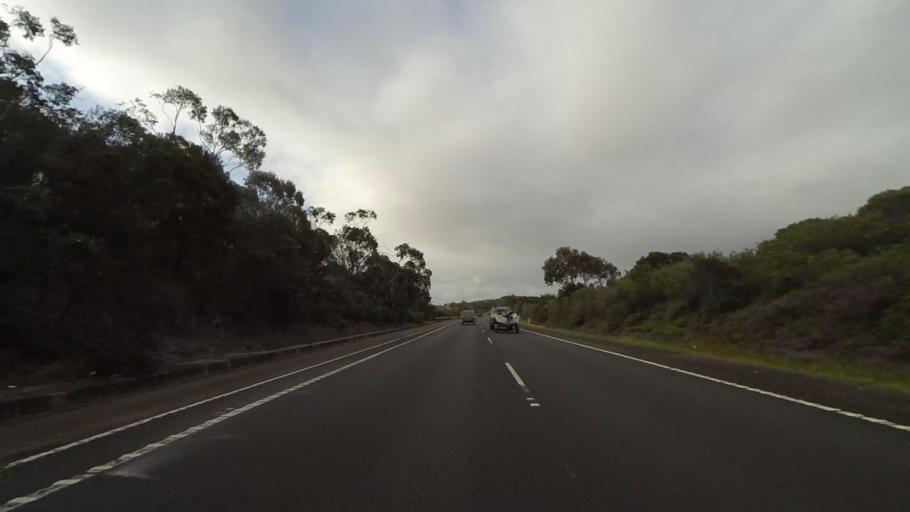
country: AU
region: New South Wales
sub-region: Wollongong
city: Bulli
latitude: -34.2720
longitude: 150.9267
